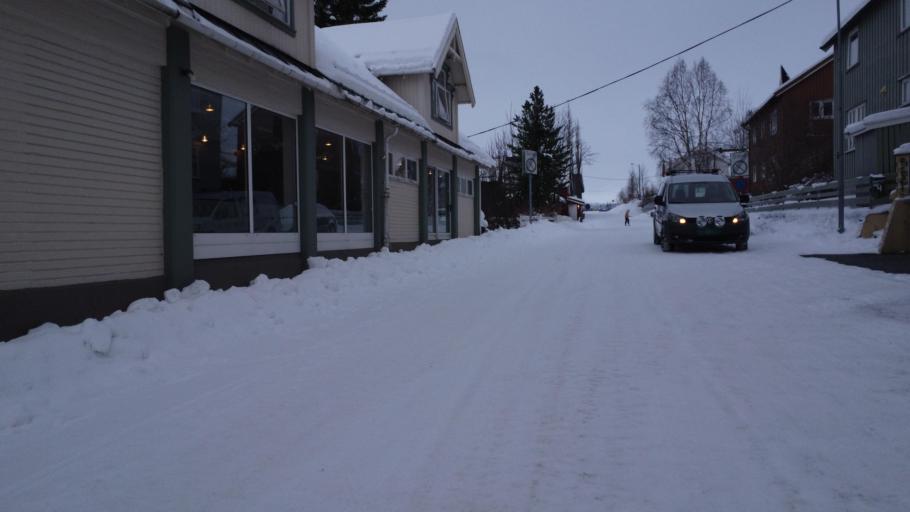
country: NO
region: Nordland
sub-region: Rana
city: Mo i Rana
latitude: 66.3128
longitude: 14.1337
